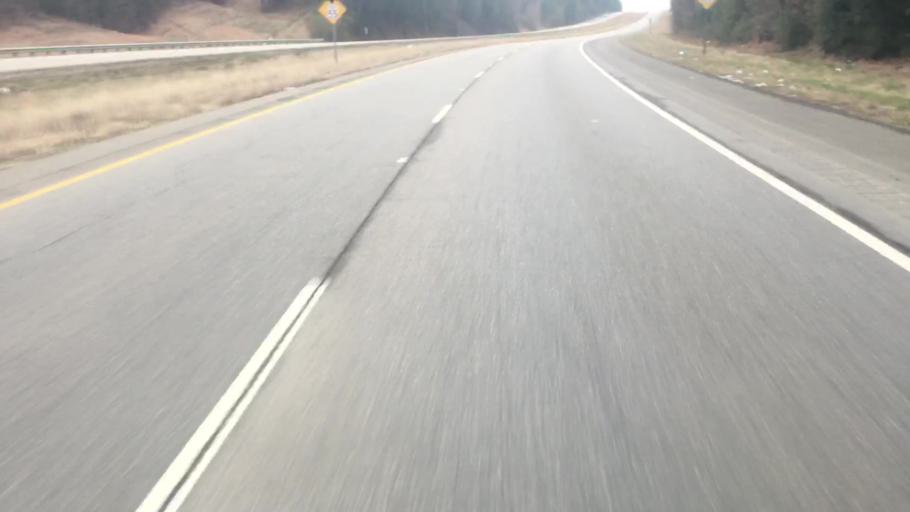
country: US
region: Alabama
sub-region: Walker County
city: Sumiton
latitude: 33.7722
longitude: -87.0732
